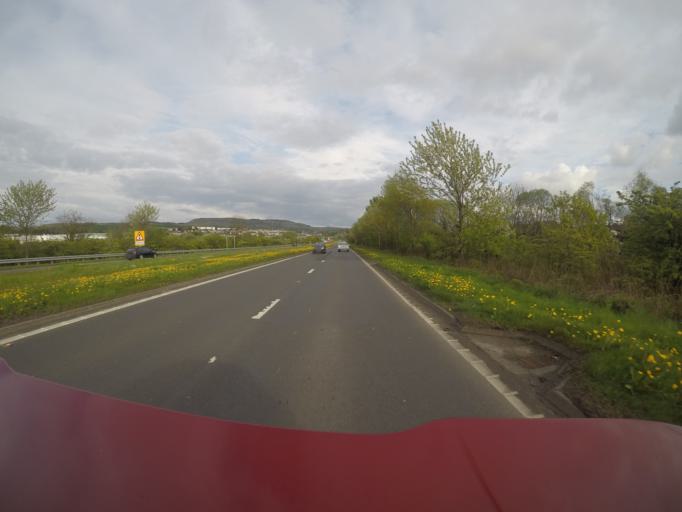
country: GB
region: Scotland
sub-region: West Dunbartonshire
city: Dumbarton
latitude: 55.9585
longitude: -4.5706
